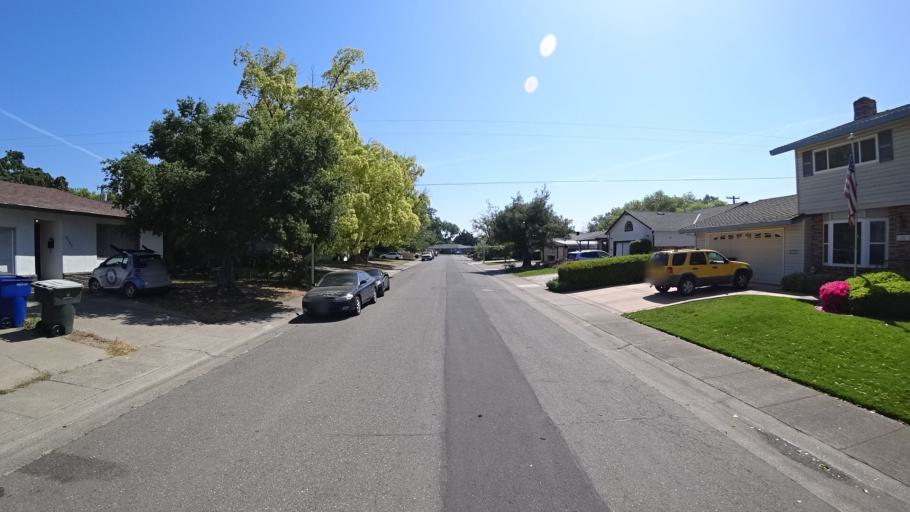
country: US
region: California
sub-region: Sacramento County
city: Parkway
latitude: 38.5157
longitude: -121.4865
